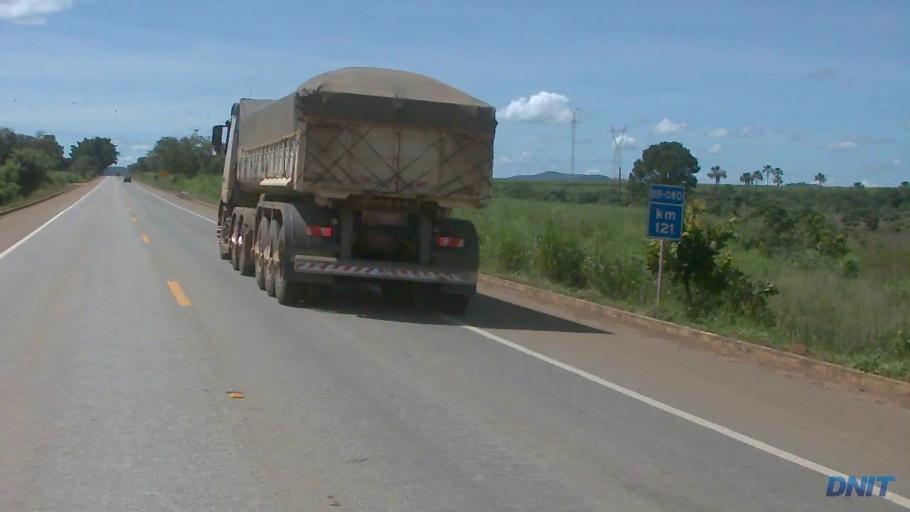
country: BR
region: Goias
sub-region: Barro Alto
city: Barro Alto
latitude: -15.0624
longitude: -48.8758
